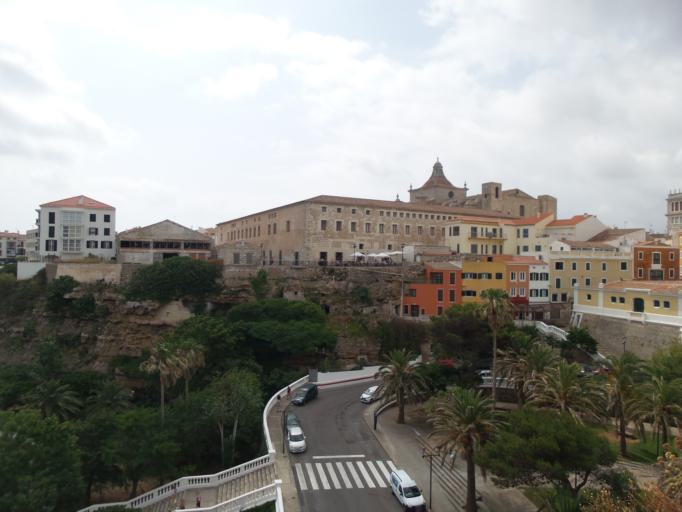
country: ES
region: Balearic Islands
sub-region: Illes Balears
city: Mao
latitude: 39.8898
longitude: 4.2655
